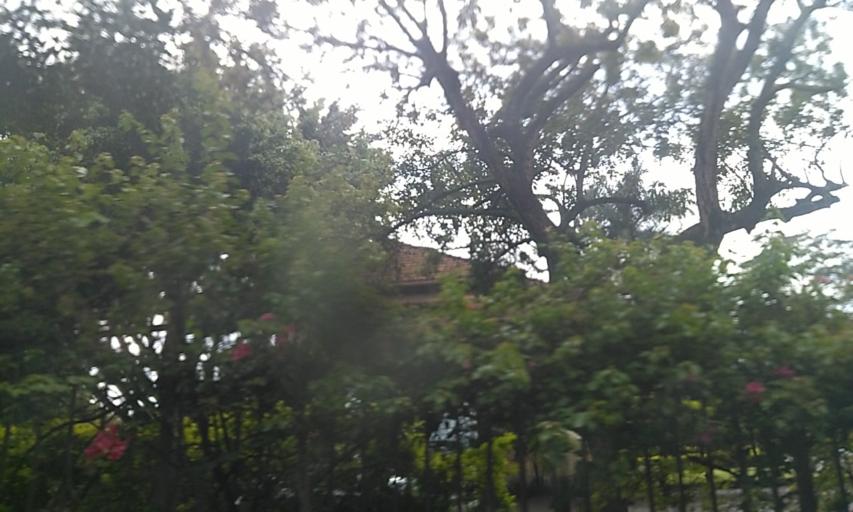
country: UG
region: Central Region
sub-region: Kampala District
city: Kampala
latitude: 0.3252
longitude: 32.5915
